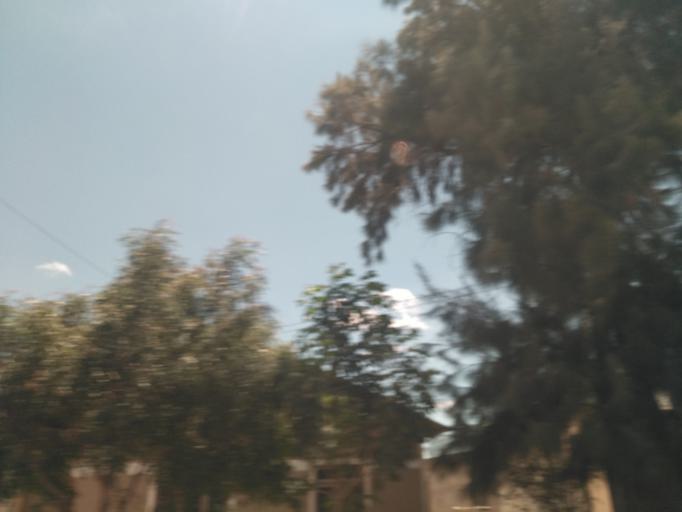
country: TZ
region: Dodoma
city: Dodoma
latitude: -6.1615
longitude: 35.7401
